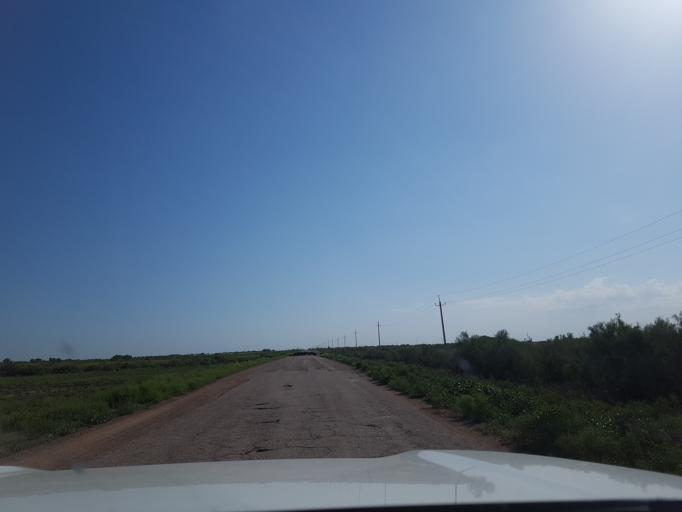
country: TM
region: Dasoguz
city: Koeneuergench
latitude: 42.0563
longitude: 58.8388
